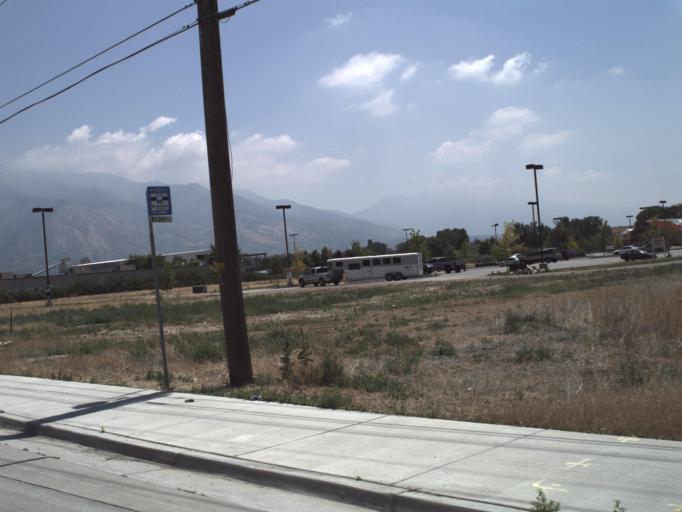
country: US
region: Utah
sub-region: Weber County
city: Marriott-Slaterville
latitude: 41.2446
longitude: -112.0094
